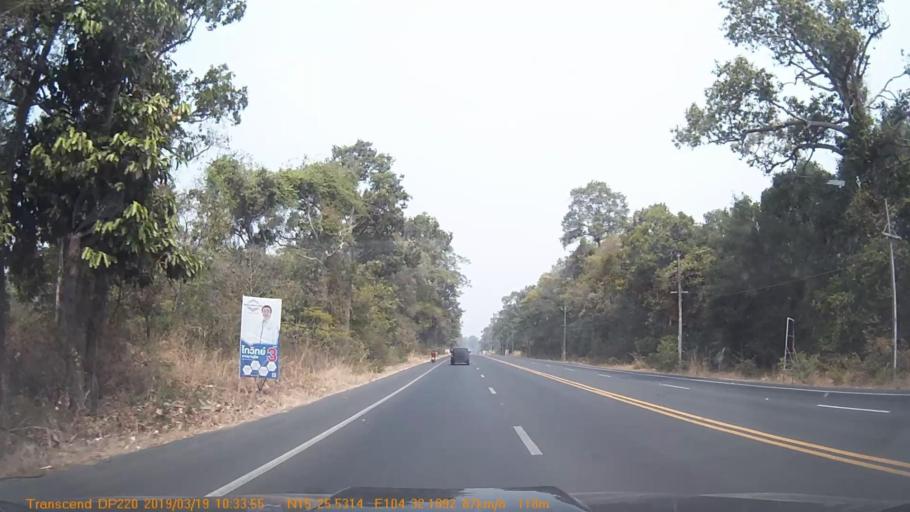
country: TH
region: Changwat Ubon Ratchathani
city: Khueang Nai
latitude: 15.4258
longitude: 104.5363
